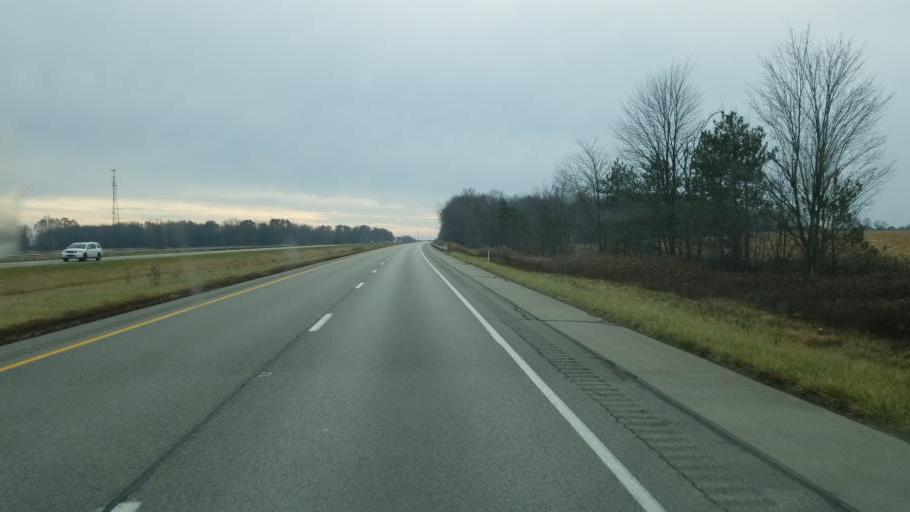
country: US
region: Pennsylvania
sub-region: Mercer County
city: Stoneboro
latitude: 41.3428
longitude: -80.1591
